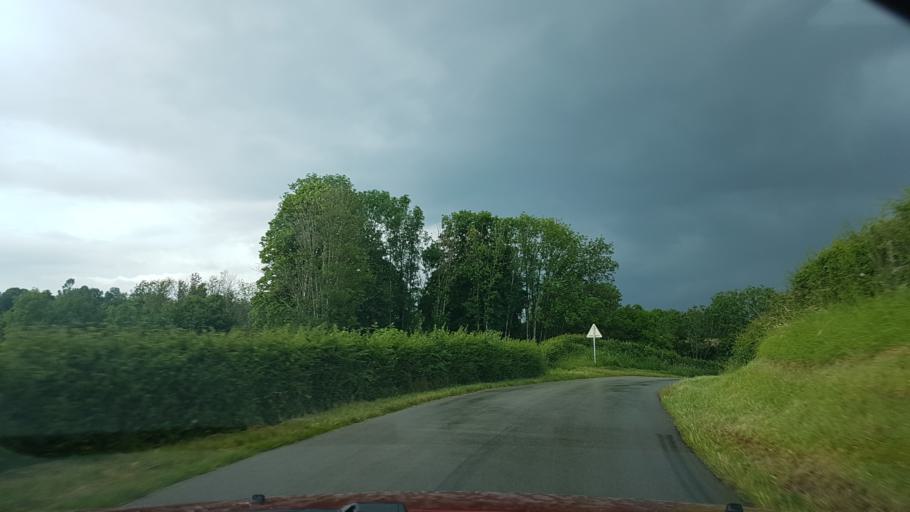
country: FR
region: Franche-Comte
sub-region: Departement du Jura
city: Clairvaux-les-Lacs
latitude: 46.5350
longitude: 5.7299
